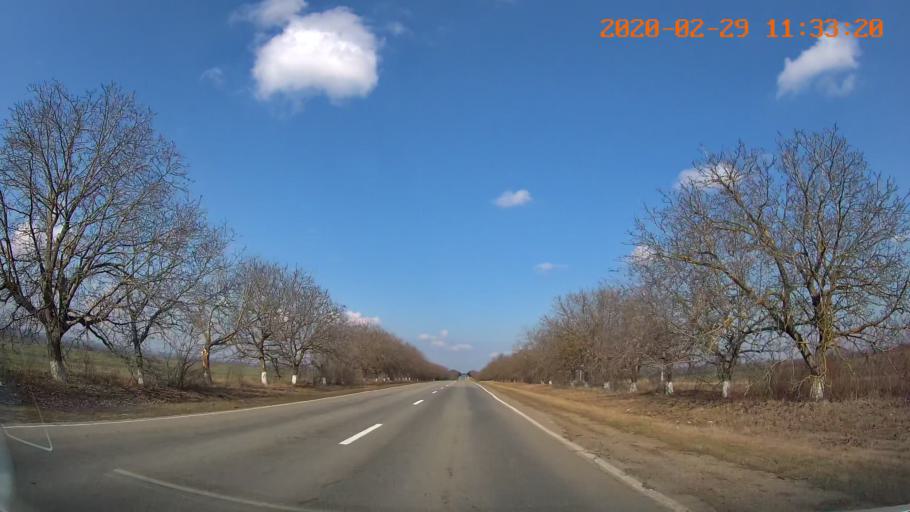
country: MD
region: Rezina
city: Saharna
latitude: 47.5502
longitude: 29.0854
